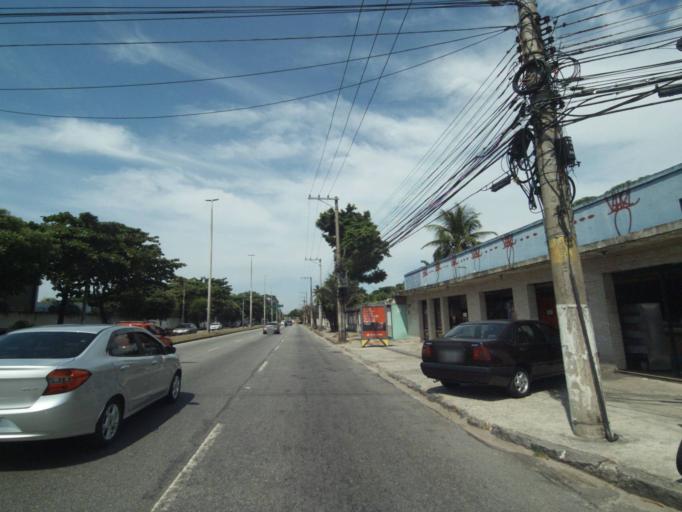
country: BR
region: Rio de Janeiro
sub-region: Rio De Janeiro
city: Rio de Janeiro
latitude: -22.8159
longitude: -43.2226
